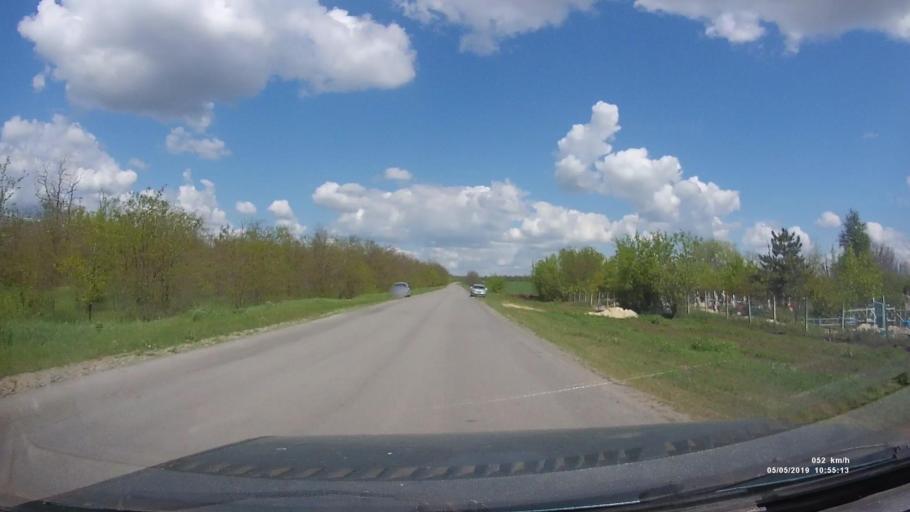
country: RU
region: Rostov
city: Ust'-Donetskiy
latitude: 47.6637
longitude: 40.8215
